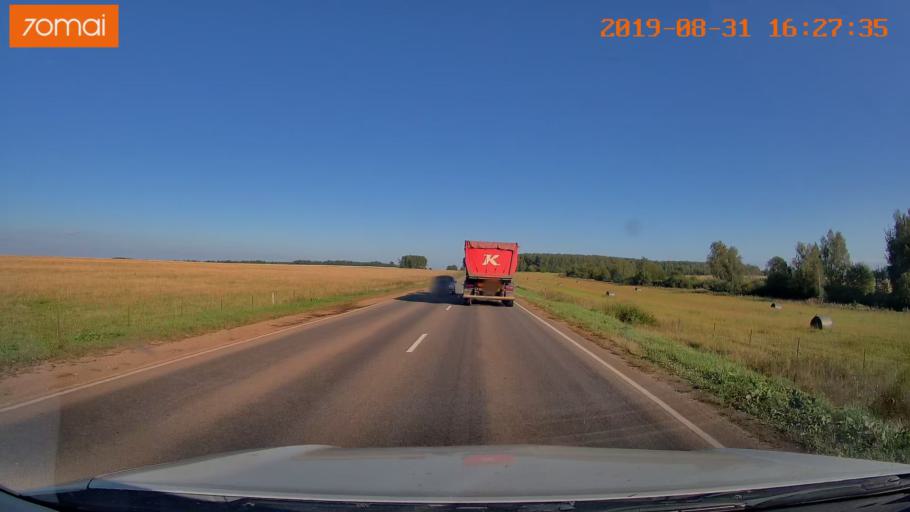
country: RU
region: Kaluga
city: Babynino
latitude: 54.5137
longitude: 35.7625
